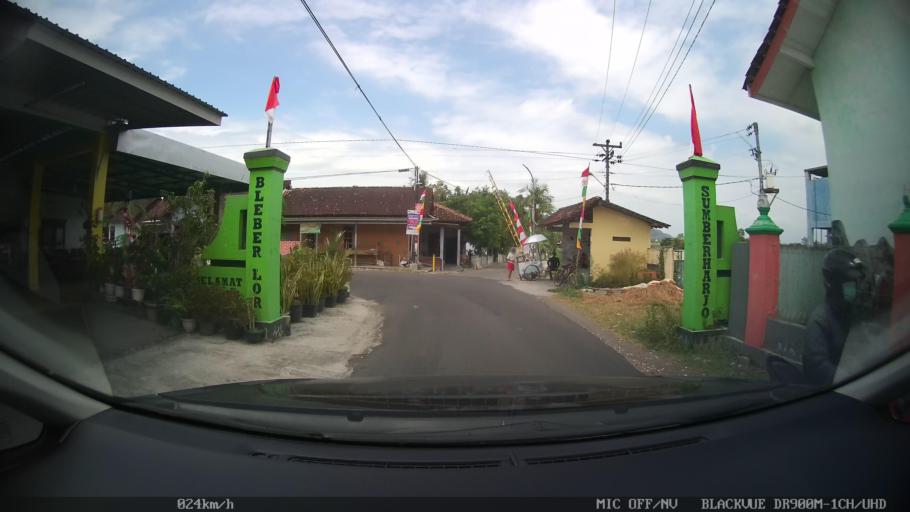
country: ID
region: Central Java
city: Candi Prambanan
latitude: -7.8136
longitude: 110.4934
